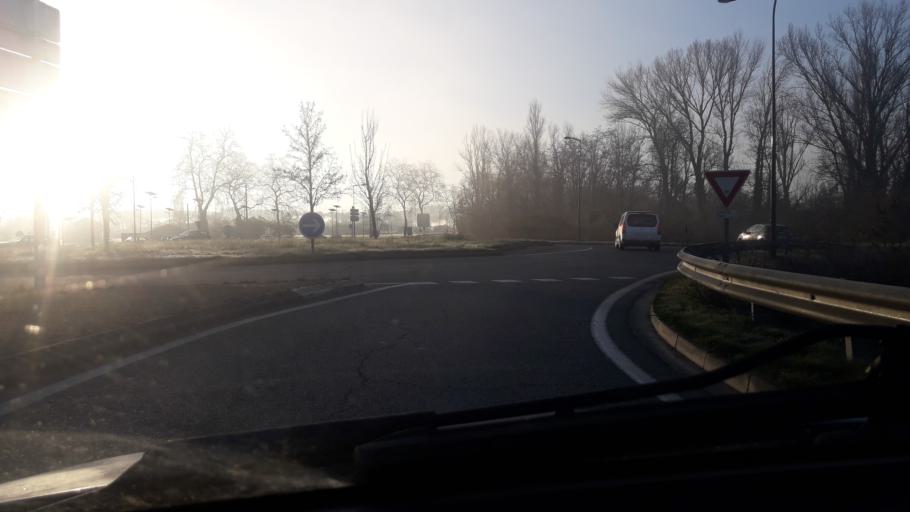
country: FR
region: Midi-Pyrenees
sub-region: Departement de la Haute-Garonne
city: Carbonne
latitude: 43.3183
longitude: 1.2186
